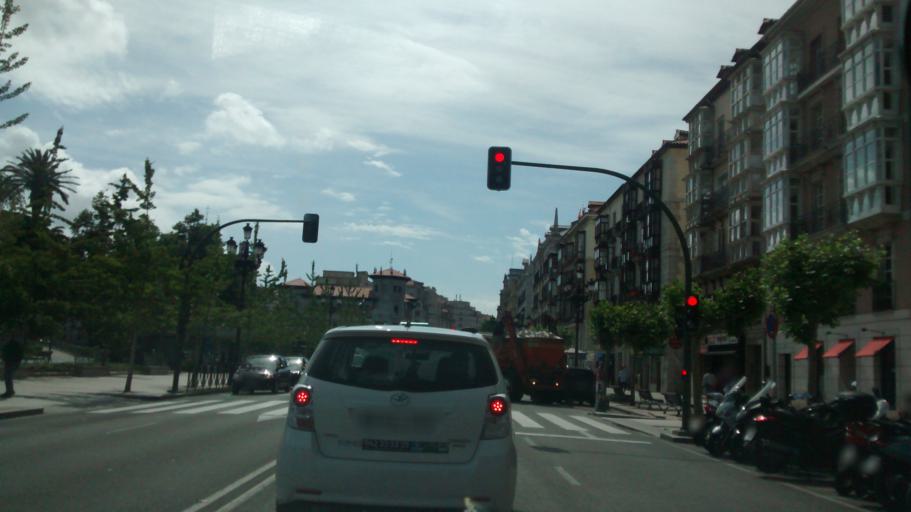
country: ES
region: Cantabria
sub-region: Provincia de Cantabria
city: Santander
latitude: 43.4618
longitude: -3.8040
